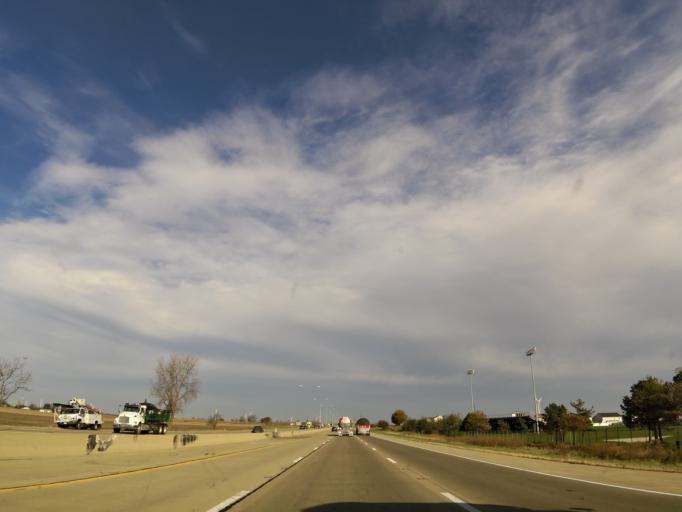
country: US
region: Illinois
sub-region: McLean County
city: Normal
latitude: 40.5216
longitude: -89.0280
